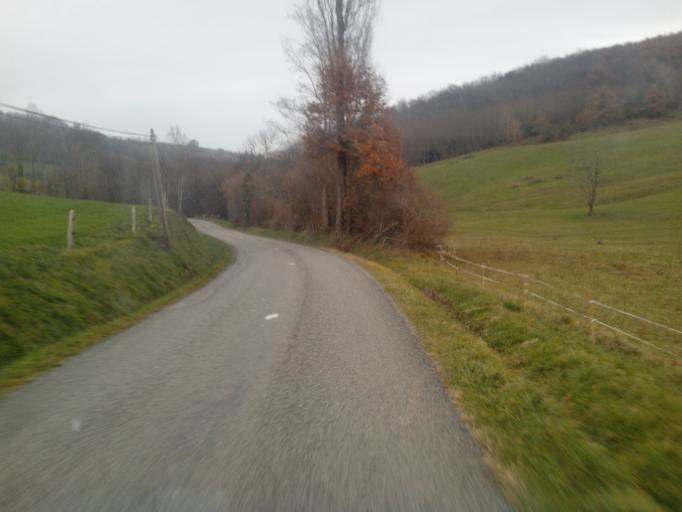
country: FR
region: Midi-Pyrenees
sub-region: Departement de l'Ariege
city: Varilhes
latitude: 43.0452
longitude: 1.5614
